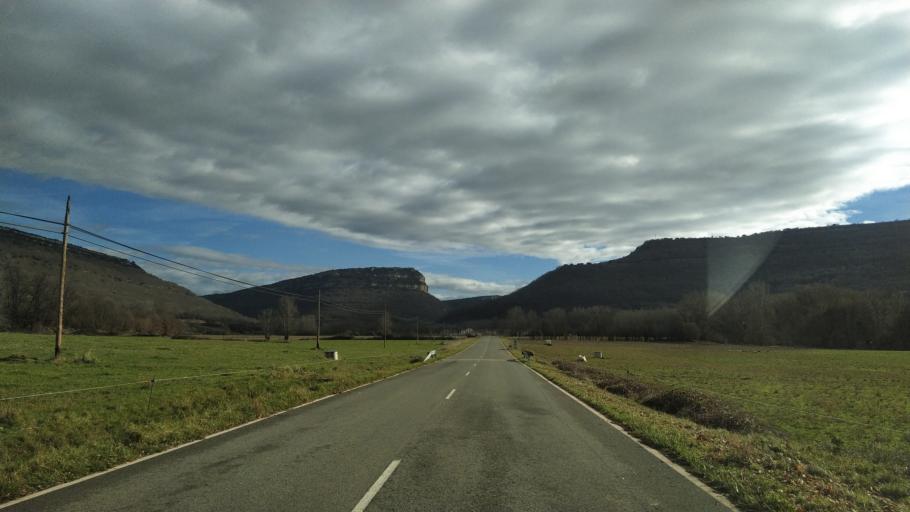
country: ES
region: Cantabria
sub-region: Provincia de Cantabria
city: San Martin de Elines
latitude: 42.8352
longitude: -3.8709
